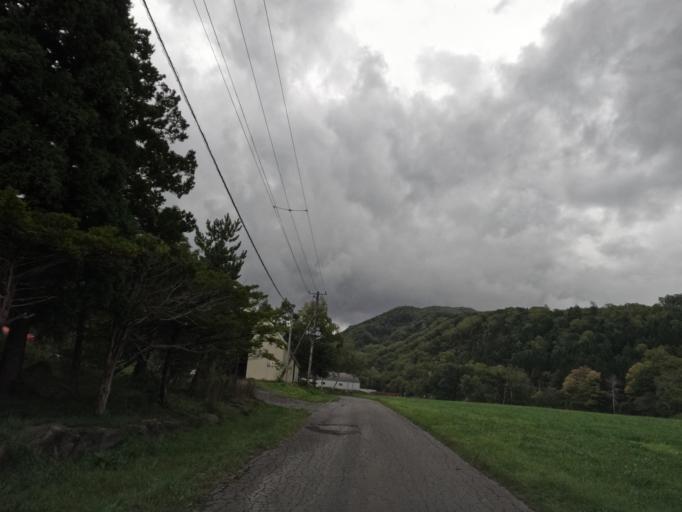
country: JP
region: Hokkaido
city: Date
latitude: 42.5009
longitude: 140.9055
